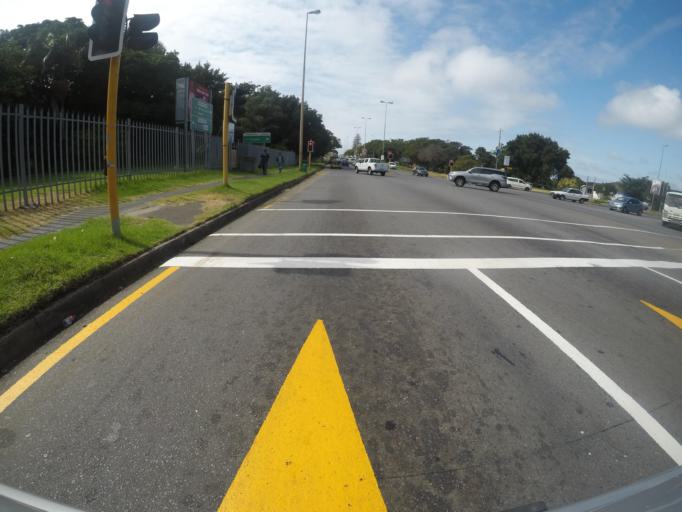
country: ZA
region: Eastern Cape
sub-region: Buffalo City Metropolitan Municipality
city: East London
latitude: -32.9951
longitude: 27.8969
